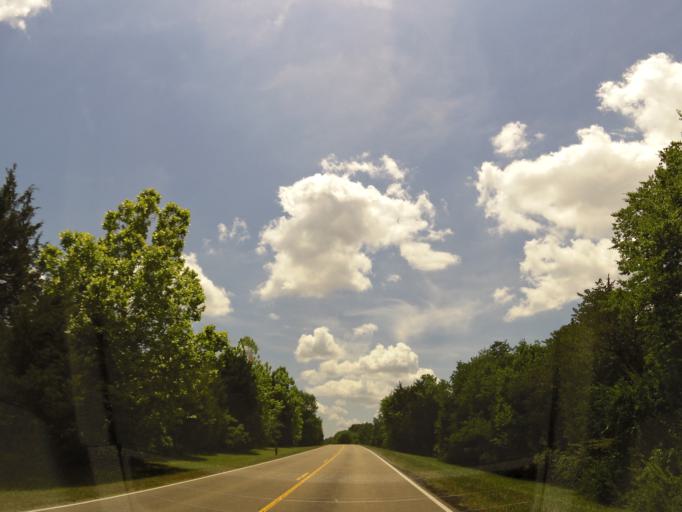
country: US
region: Mississippi
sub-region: Lee County
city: Tupelo
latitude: 34.2674
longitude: -88.7504
